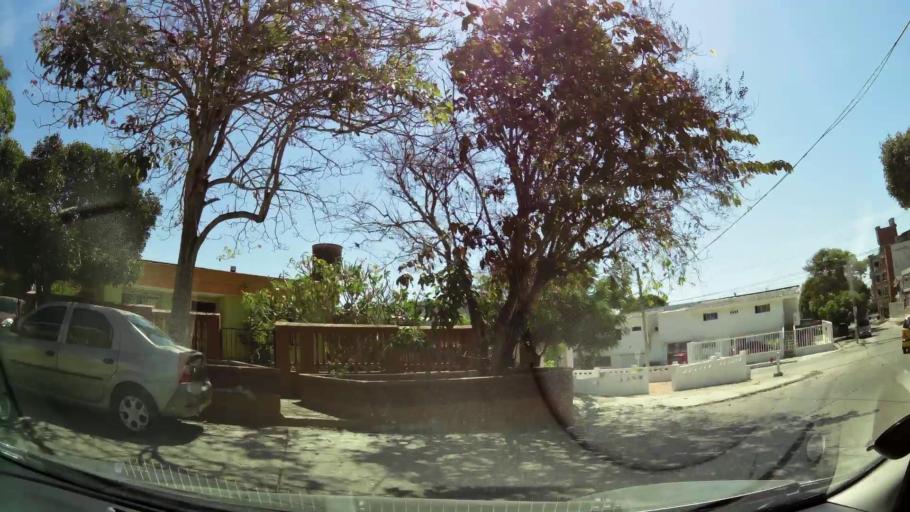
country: CO
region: Atlantico
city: Barranquilla
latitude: 10.9881
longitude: -74.8173
